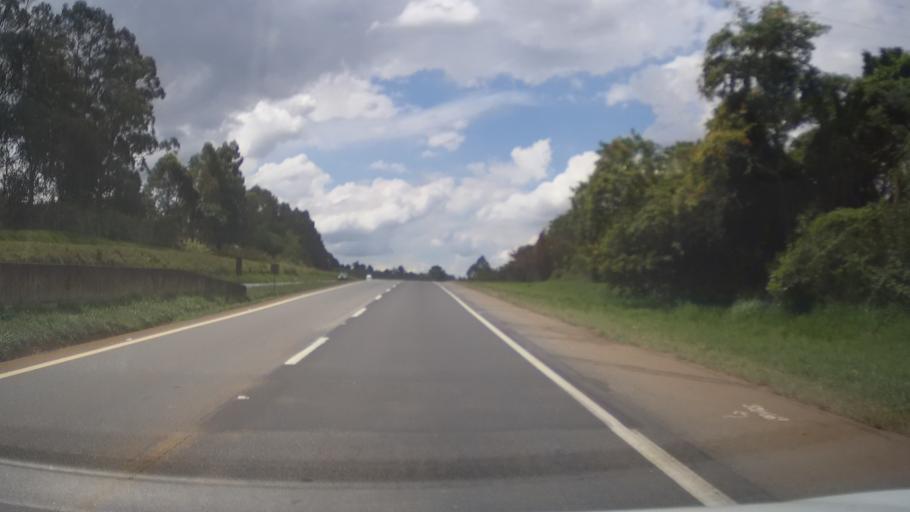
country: BR
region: Minas Gerais
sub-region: Nepomuceno
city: Nepomuceno
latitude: -21.2536
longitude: -45.1387
